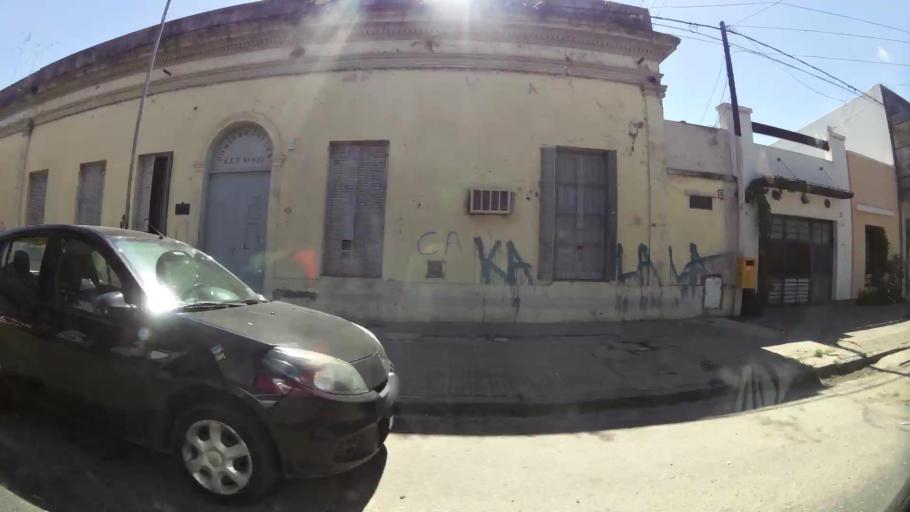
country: AR
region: Santa Fe
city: Santa Fe de la Vera Cruz
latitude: -31.6412
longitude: -60.6888
